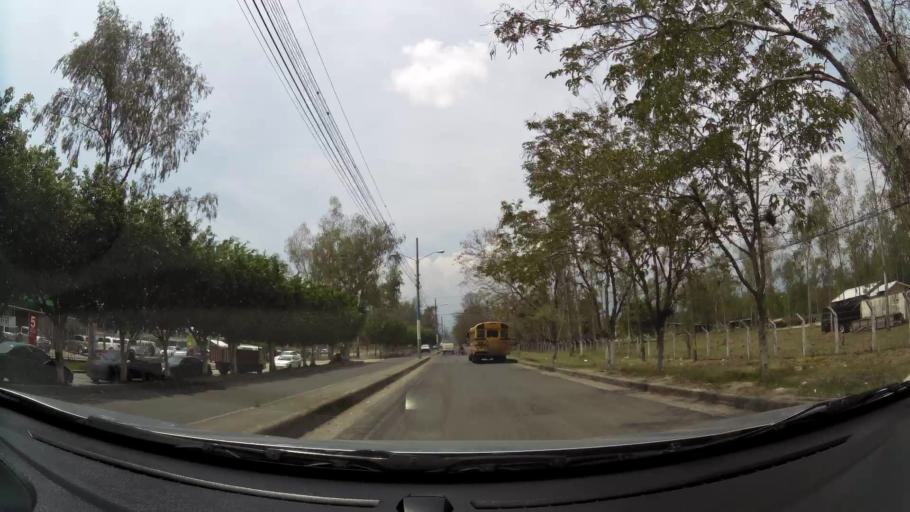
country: HN
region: Comayagua
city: Siguatepeque
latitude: 14.5833
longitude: -87.8353
